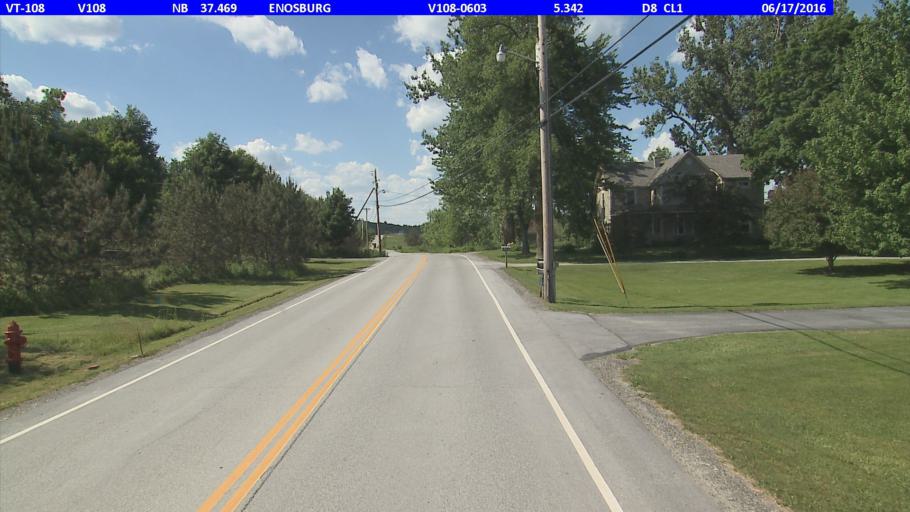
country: US
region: Vermont
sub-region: Franklin County
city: Enosburg Falls
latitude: 44.9173
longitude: -72.8058
